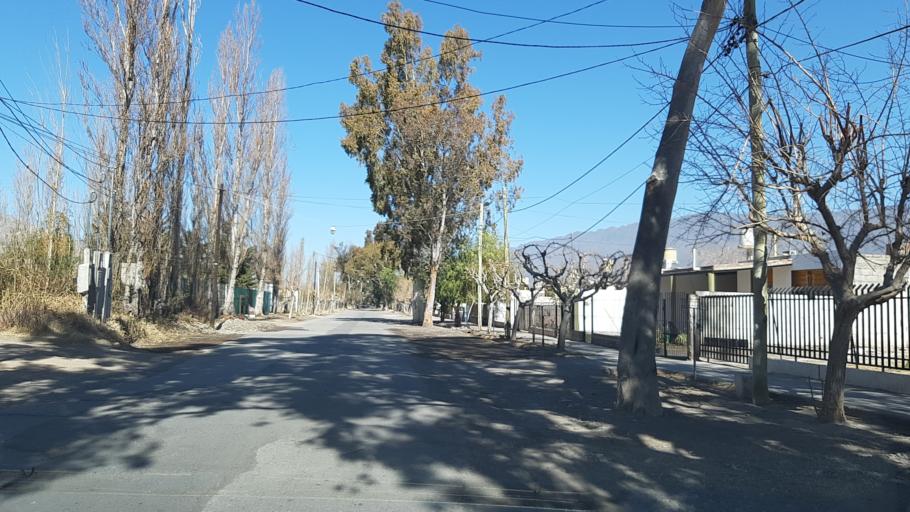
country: AR
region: San Juan
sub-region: Departamento de Zonda
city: Zonda
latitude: -31.5469
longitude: -68.7262
